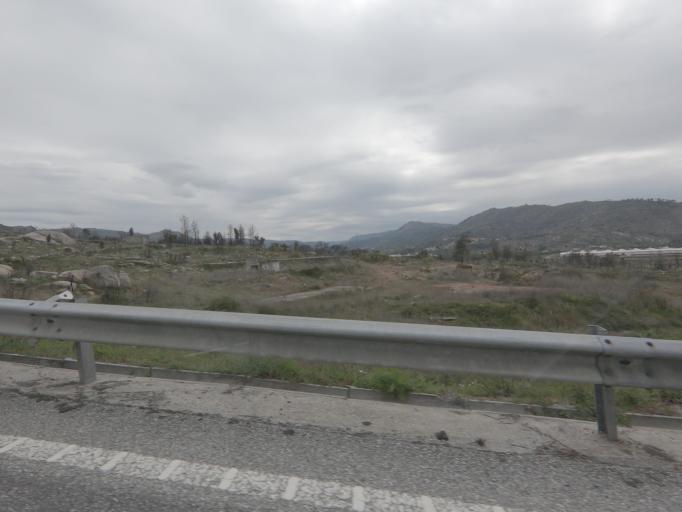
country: PT
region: Guarda
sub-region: Guarda
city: Guarda
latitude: 40.6205
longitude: -7.2894
